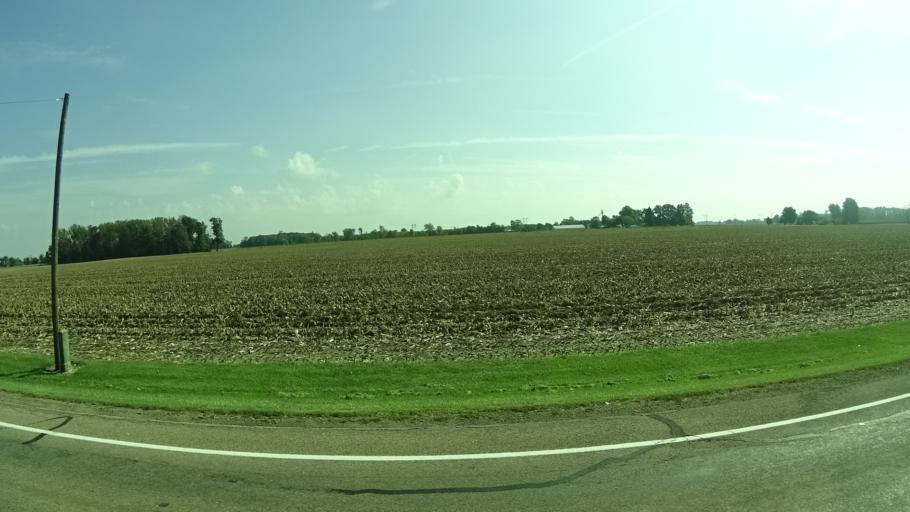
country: US
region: Indiana
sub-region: Madison County
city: Ingalls
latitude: 40.0045
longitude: -85.8432
